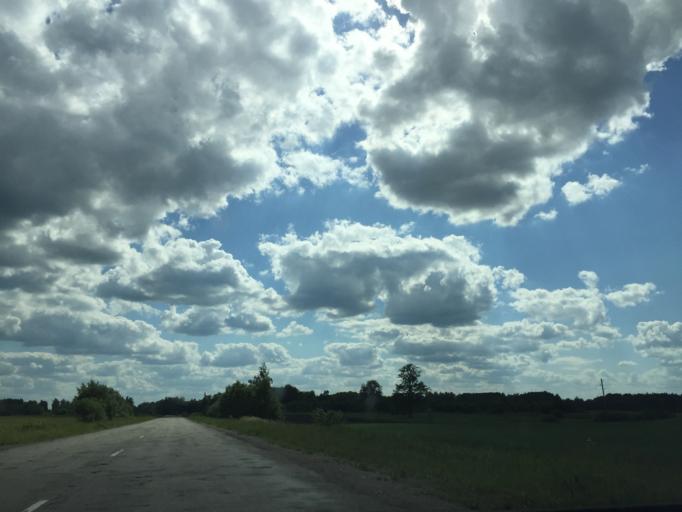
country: LV
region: Tukuma Rajons
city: Tukums
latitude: 56.8704
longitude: 23.0658
